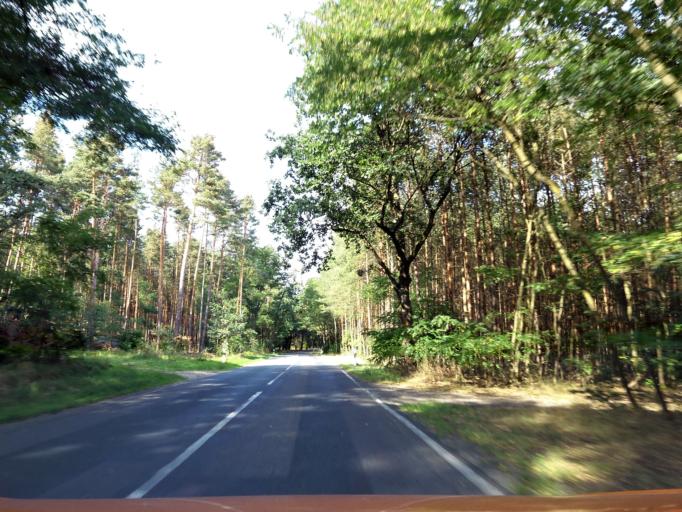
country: DE
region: Brandenburg
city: Michendorf
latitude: 52.2923
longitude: 13.1130
